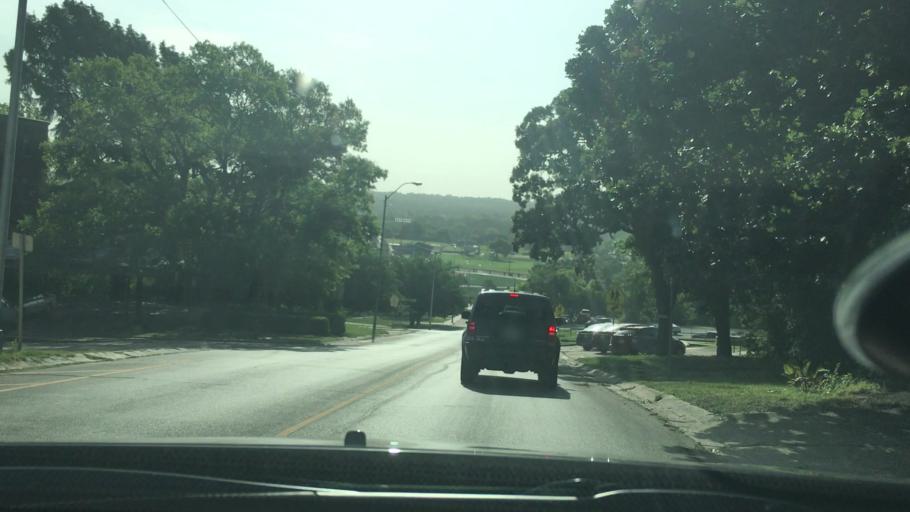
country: US
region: Oklahoma
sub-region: Pontotoc County
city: Ada
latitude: 34.7714
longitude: -96.6641
